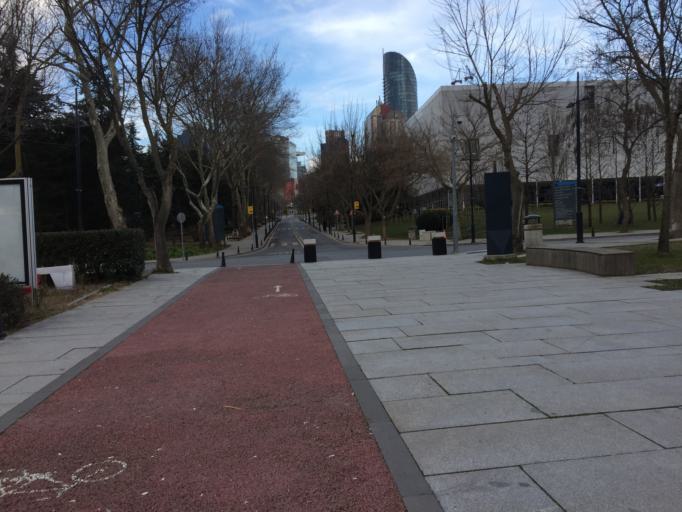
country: TR
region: Istanbul
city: Sisli
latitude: 41.1045
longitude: 29.0229
